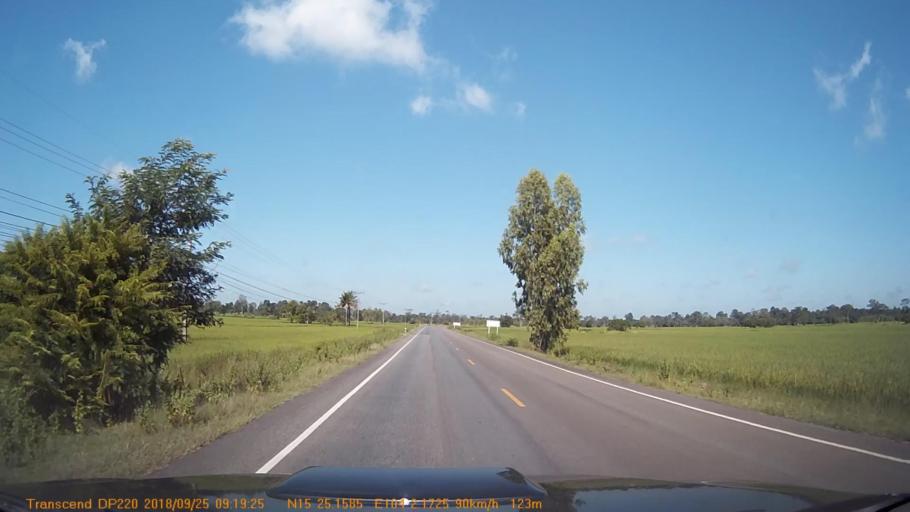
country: TH
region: Sisaket
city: Sila Lat
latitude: 15.4192
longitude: 104.0366
